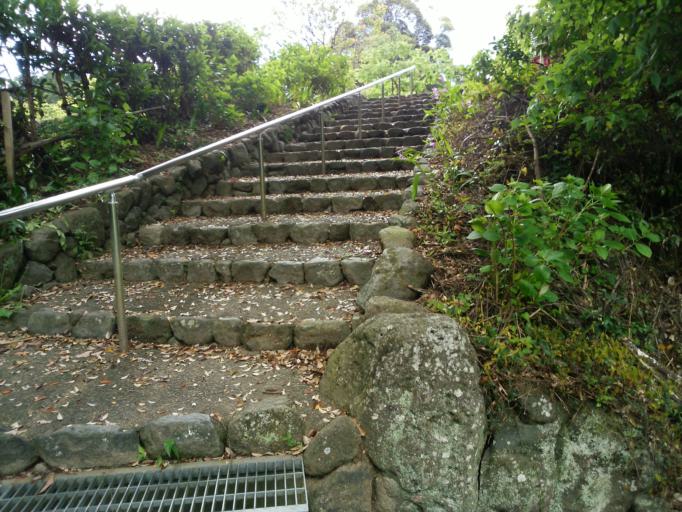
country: JP
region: Shizuoka
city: Kakegawa
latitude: 34.7841
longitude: 138.0162
